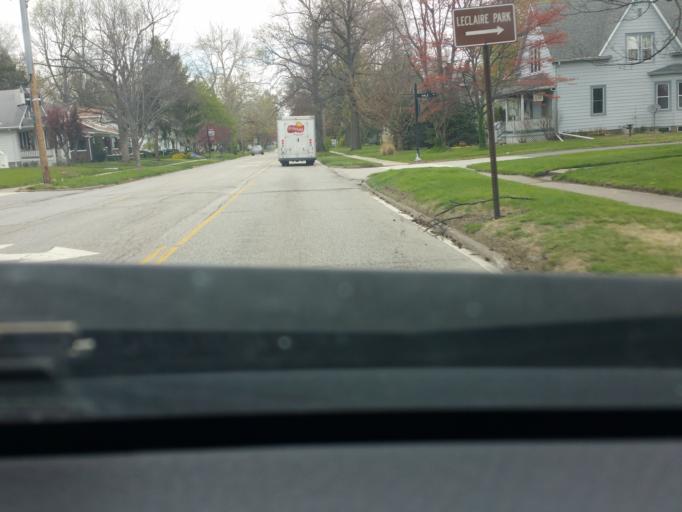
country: US
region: Illinois
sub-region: Madison County
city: Edwardsville
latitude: 38.7989
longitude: -89.9510
